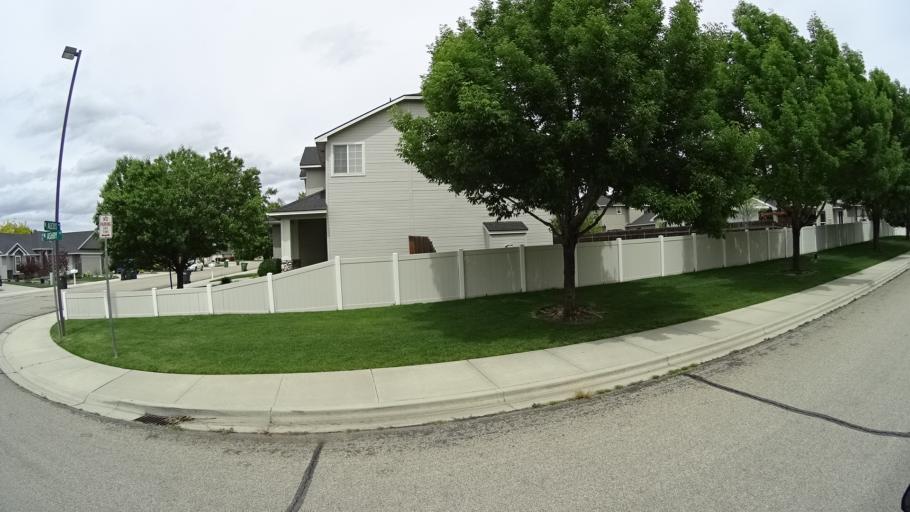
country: US
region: Idaho
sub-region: Ada County
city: Meridian
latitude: 43.6375
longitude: -116.3978
